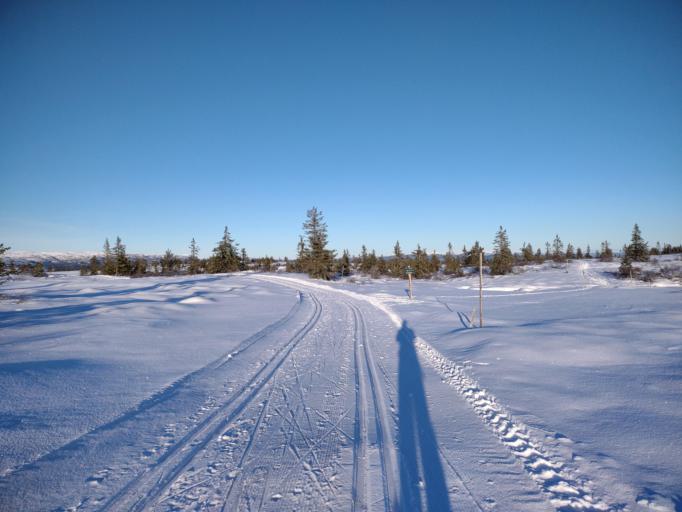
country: NO
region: Buskerud
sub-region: Rollag
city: Rollag
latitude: 59.8003
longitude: 9.3435
